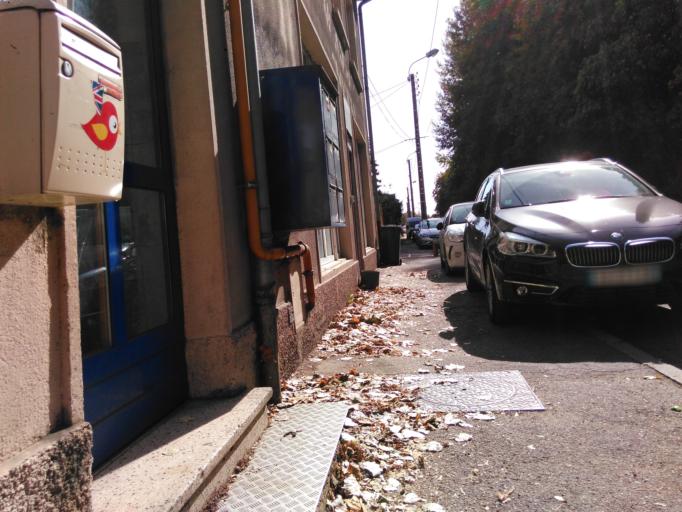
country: FR
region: Lorraine
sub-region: Departement de la Moselle
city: Thionville
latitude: 49.3756
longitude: 6.1694
